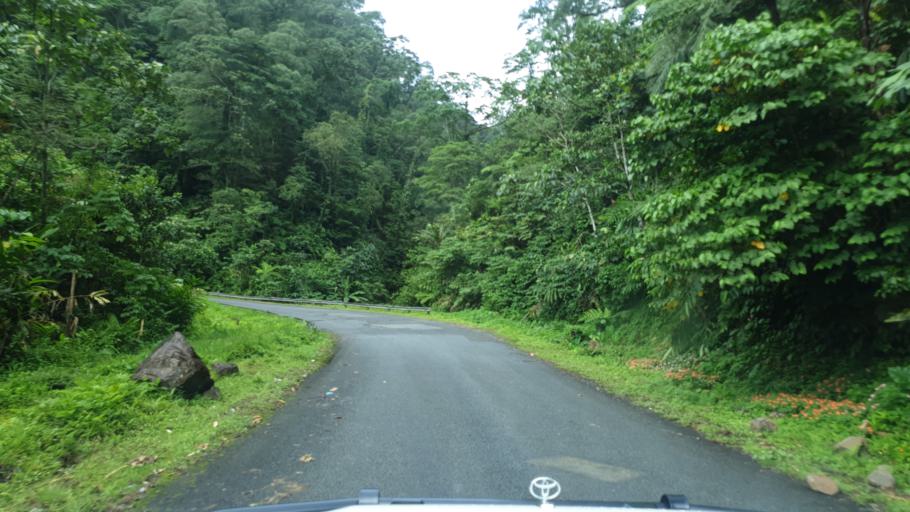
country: PG
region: Bougainville
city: Panguna
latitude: -6.2870
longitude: 155.4638
